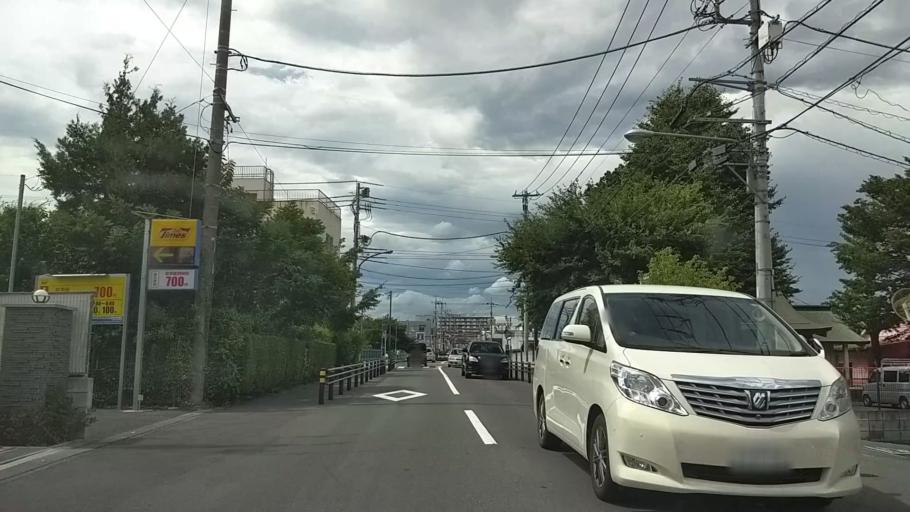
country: JP
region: Tokyo
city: Hachioji
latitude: 35.6526
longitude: 139.3009
